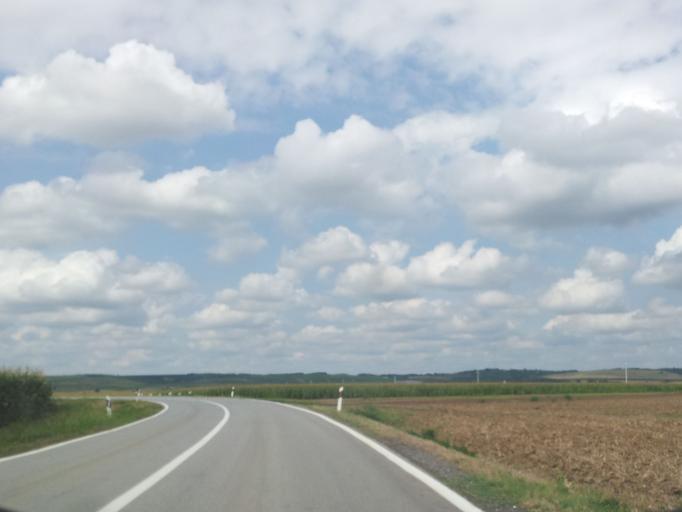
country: HR
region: Osjecko-Baranjska
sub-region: Grad Osijek
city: Karanac
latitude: 45.7456
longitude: 18.7174
